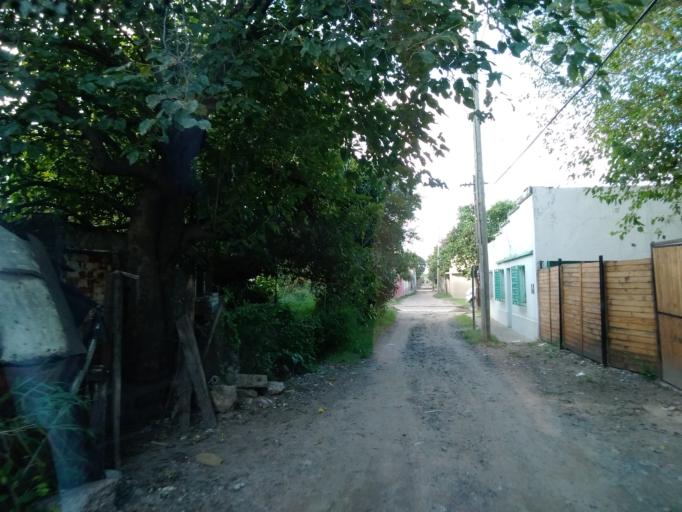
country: AR
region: Corrientes
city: Corrientes
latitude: -27.4771
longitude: -58.8082
